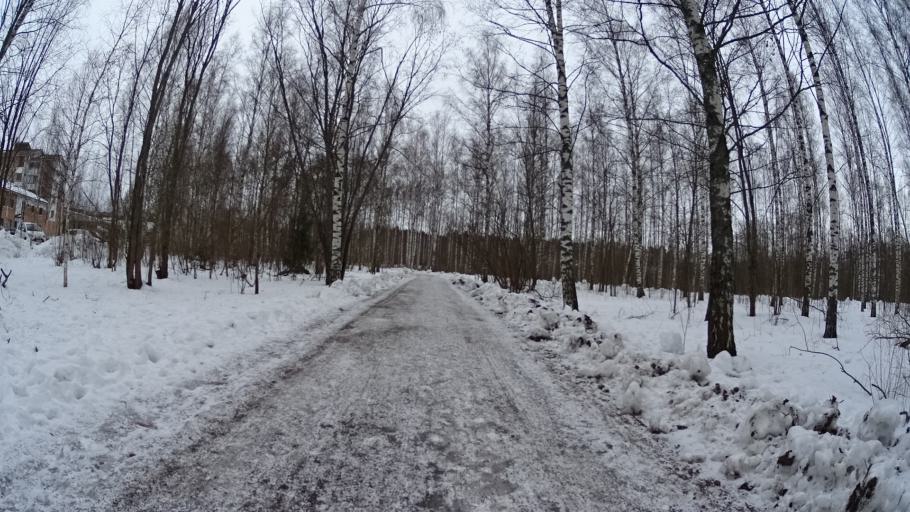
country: FI
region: Uusimaa
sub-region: Helsinki
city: Teekkarikylae
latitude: 60.2570
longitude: 24.8608
